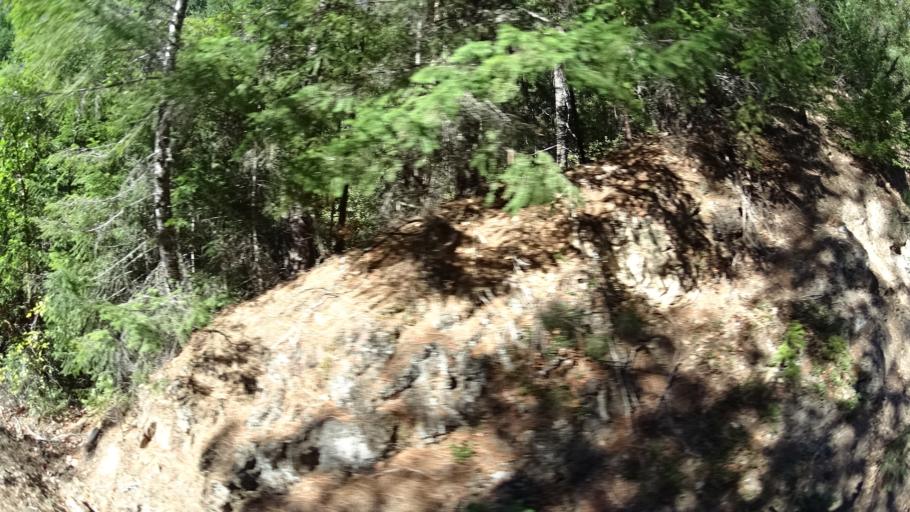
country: US
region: California
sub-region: Trinity County
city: Weaverville
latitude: 41.2263
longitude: -123.0179
